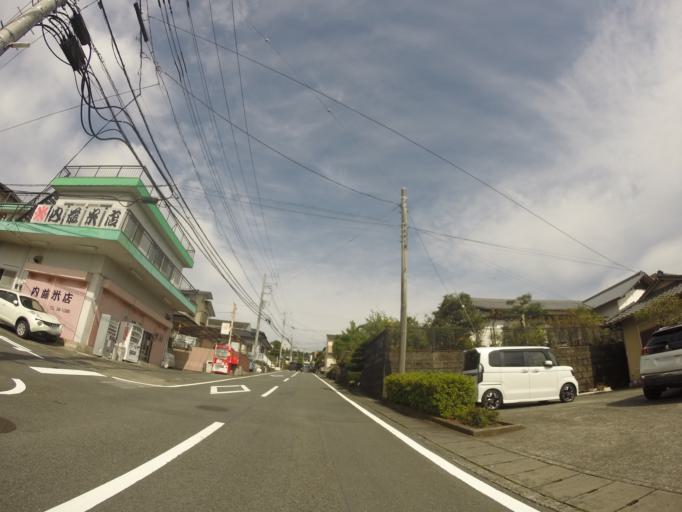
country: JP
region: Shizuoka
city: Fuji
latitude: 35.1916
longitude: 138.6939
